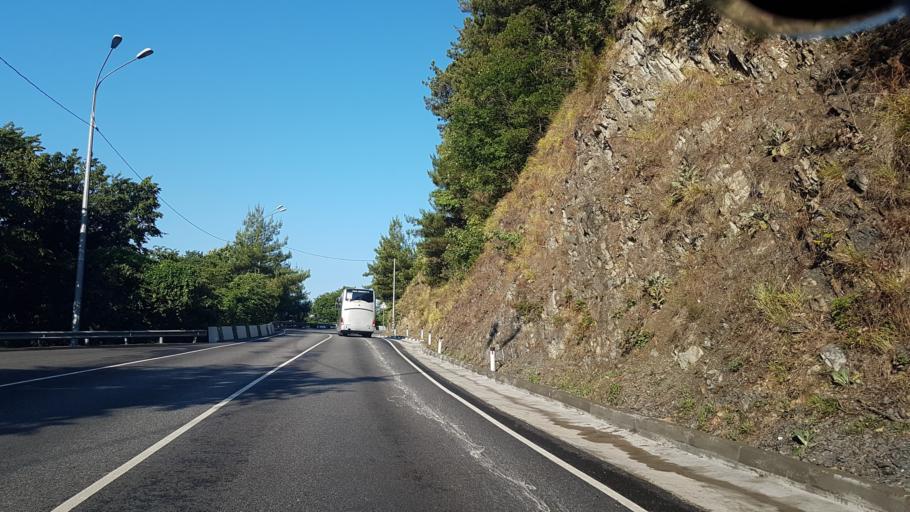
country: RU
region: Krasnodarskiy
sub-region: Sochi City
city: Lazarevskoye
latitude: 43.8390
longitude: 39.4198
